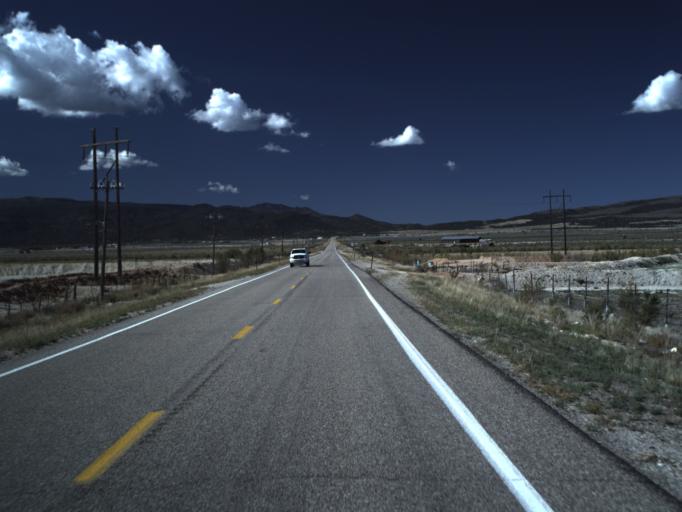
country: US
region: Utah
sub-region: Iron County
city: Cedar City
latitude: 37.6634
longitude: -113.2066
